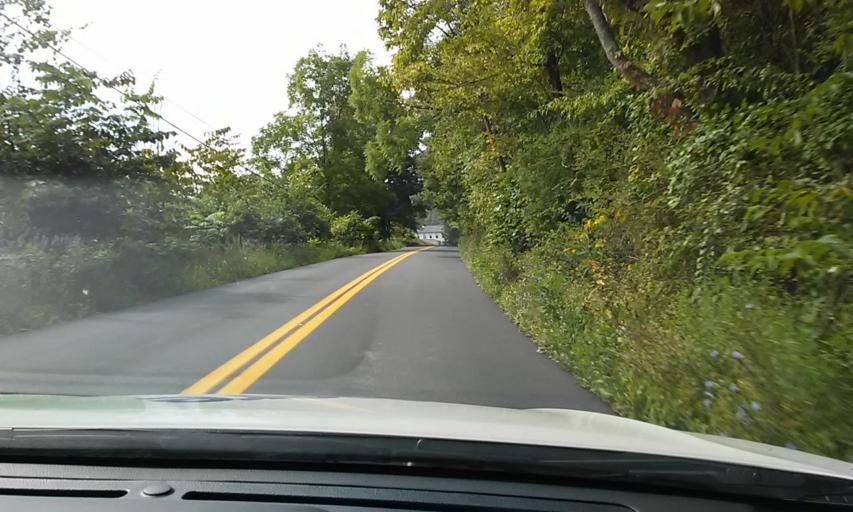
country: US
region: West Virginia
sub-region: Monongalia County
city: Star City
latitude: 39.6534
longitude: -80.0990
